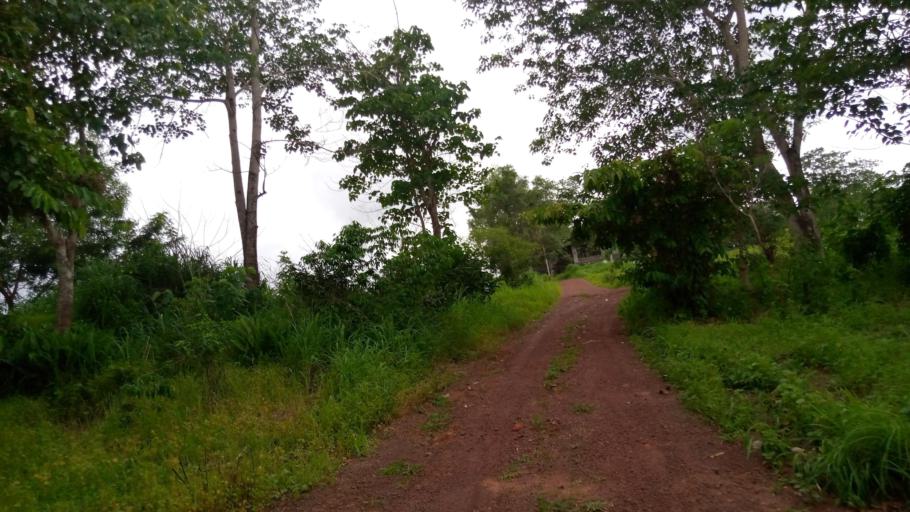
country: SL
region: Southern Province
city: Moyamba
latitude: 8.1614
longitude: -12.4452
